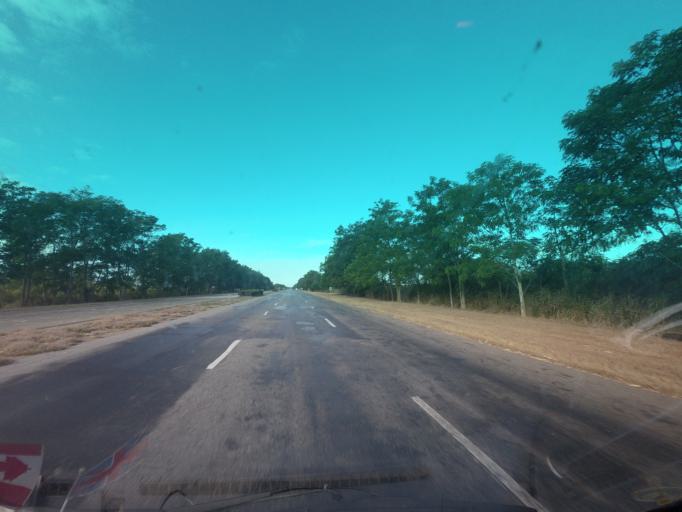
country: CU
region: Cienfuegos
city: Rodas
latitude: 22.4435
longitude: -80.4669
